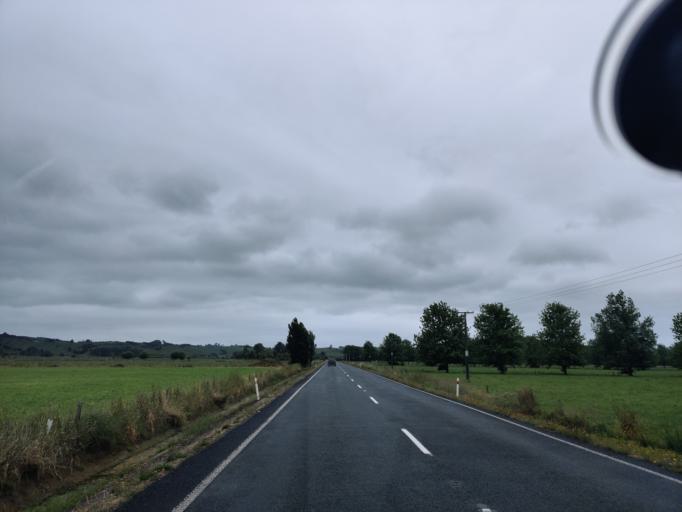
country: NZ
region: Northland
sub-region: Kaipara District
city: Dargaville
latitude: -36.1197
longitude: 174.0848
